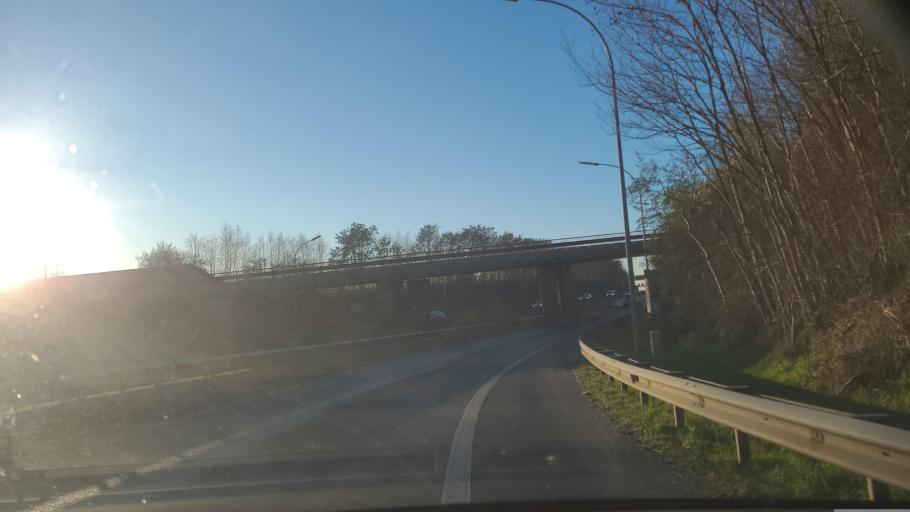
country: LU
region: Luxembourg
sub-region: Canton de Luxembourg
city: Strassen
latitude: 49.6306
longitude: 6.0659
